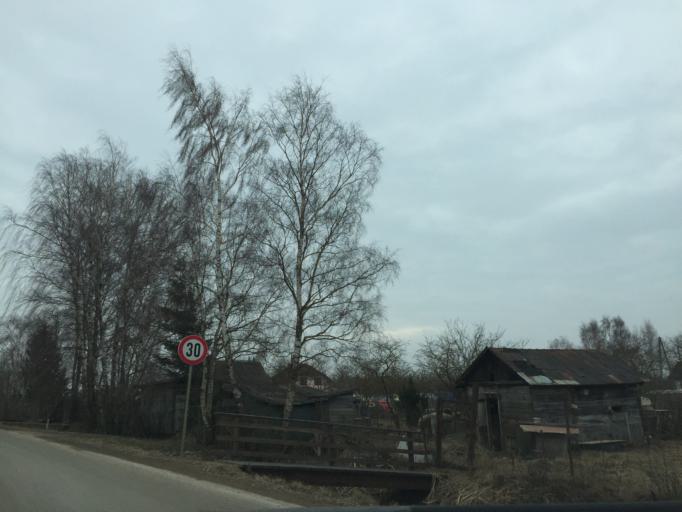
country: LV
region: Marupe
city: Marupe
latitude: 56.8805
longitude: 24.0554
